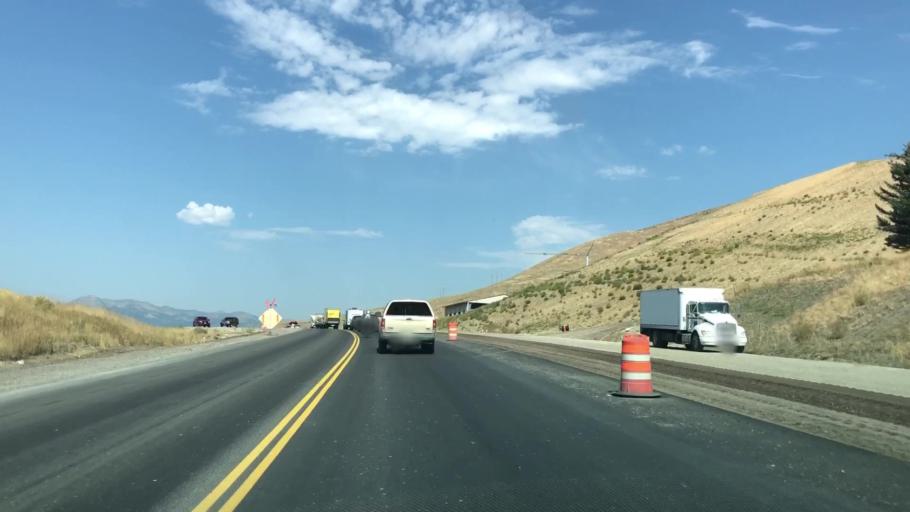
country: US
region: Wyoming
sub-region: Teton County
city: South Park
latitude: 43.3989
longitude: -110.7510
